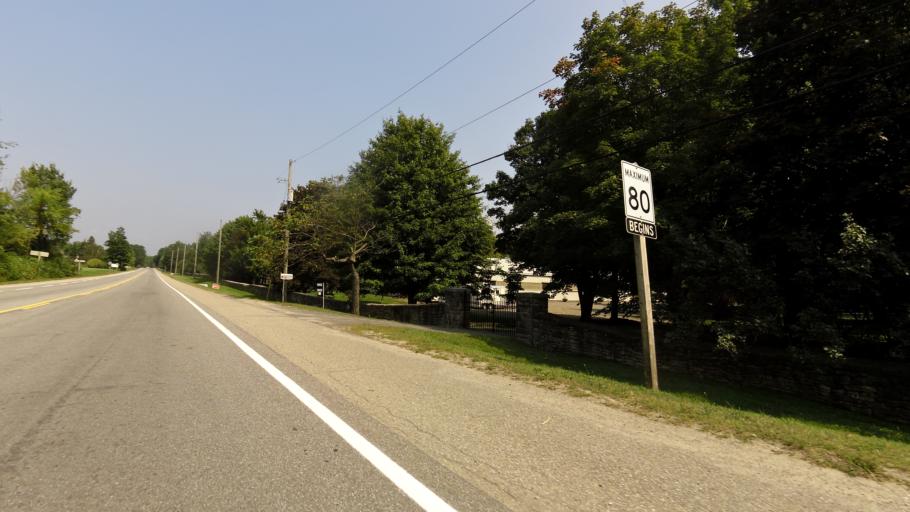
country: CA
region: Ontario
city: Brockville
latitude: 44.6117
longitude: -75.6511
